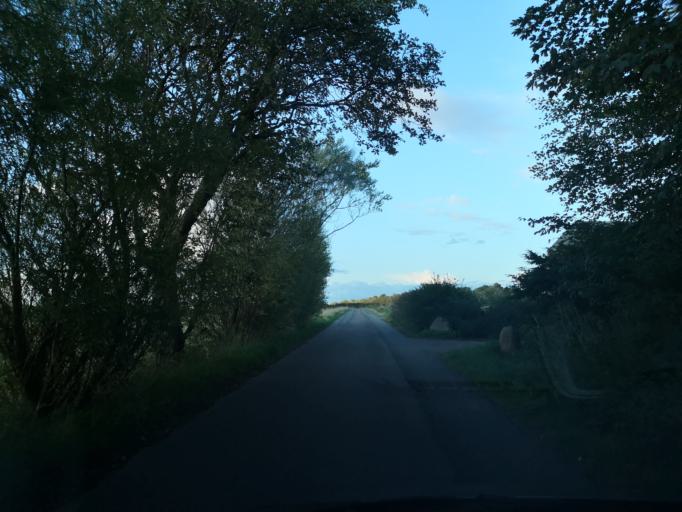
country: DK
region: Central Jutland
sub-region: Ringkobing-Skjern Kommune
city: Videbaek
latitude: 56.0298
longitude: 8.5679
